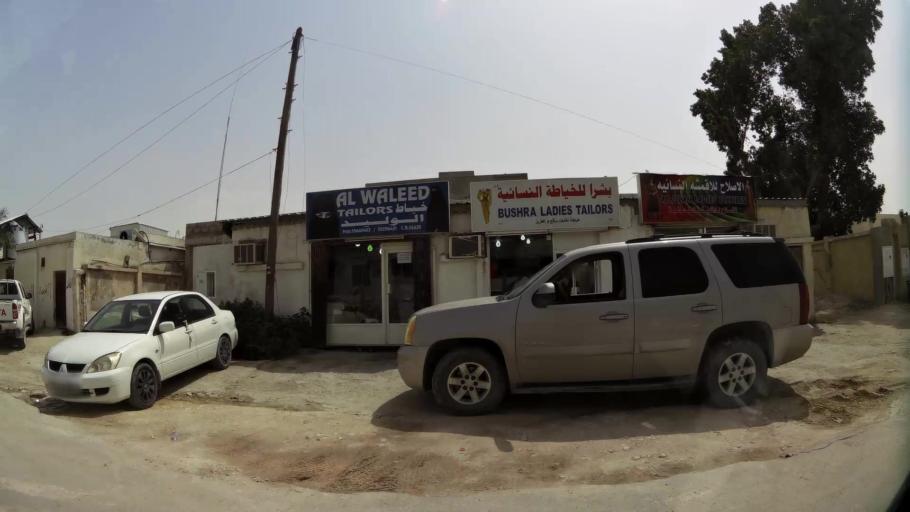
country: QA
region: Baladiyat ar Rayyan
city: Ar Rayyan
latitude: 25.2356
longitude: 51.4282
